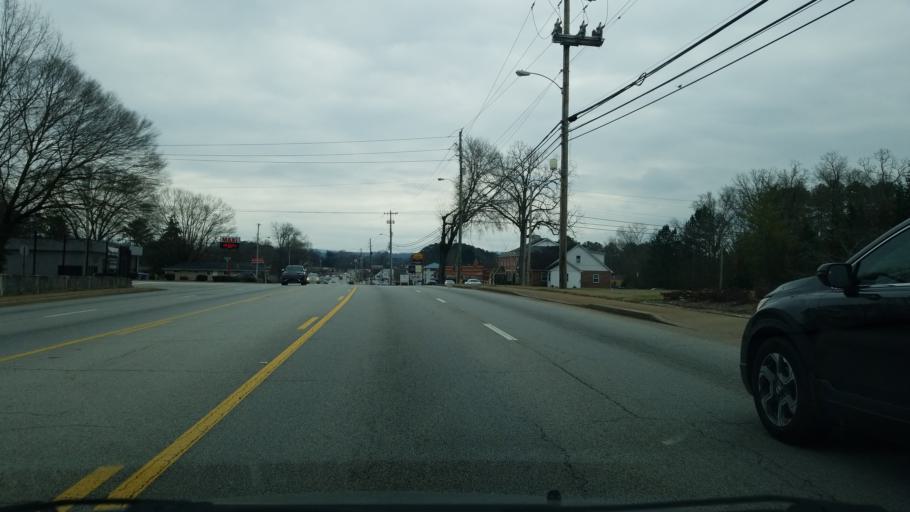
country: US
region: Tennessee
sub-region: Hamilton County
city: East Brainerd
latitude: 35.0142
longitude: -85.1621
